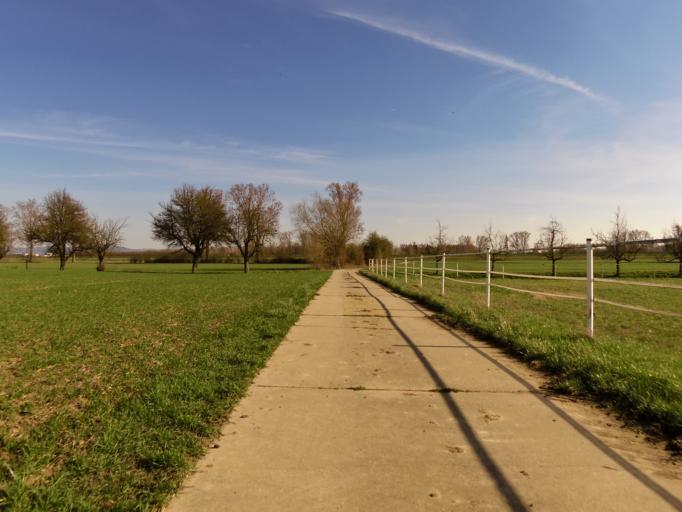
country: DE
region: Hesse
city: Biebesheim
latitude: 49.7749
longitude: 8.4472
